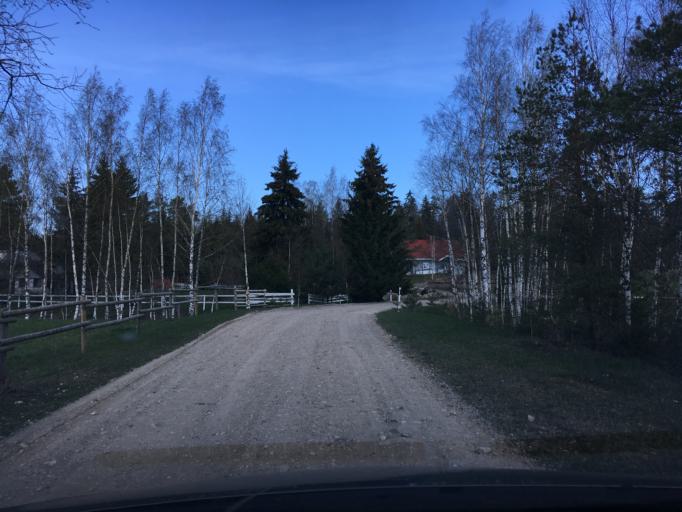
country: EE
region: Harju
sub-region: Raasiku vald
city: Raasiku
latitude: 59.2104
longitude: 25.1725
